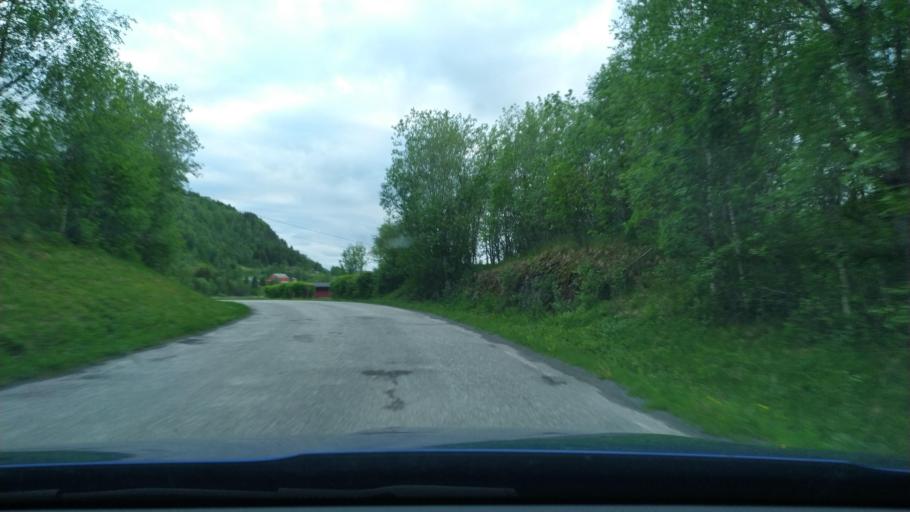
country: NO
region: Troms
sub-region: Lenvik
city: Finnsnes
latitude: 69.1366
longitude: 17.9015
